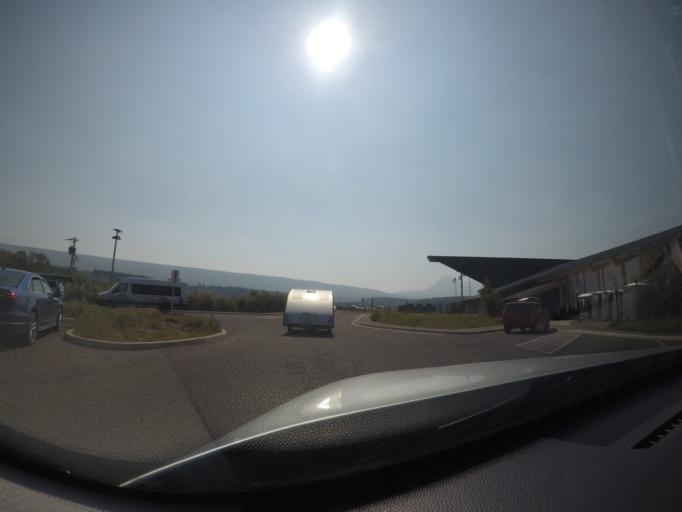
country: US
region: Montana
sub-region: Glacier County
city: North Browning
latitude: 48.7478
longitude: -113.4390
